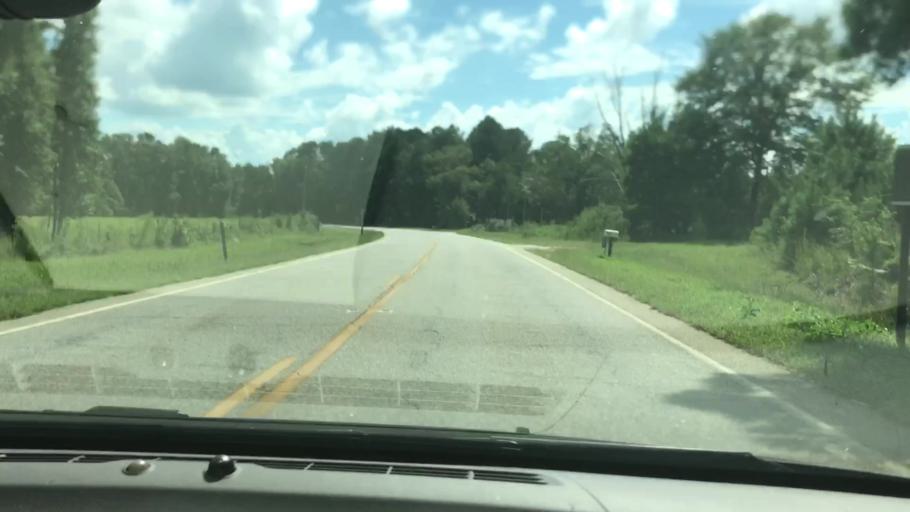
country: US
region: Georgia
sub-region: Clay County
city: Fort Gaines
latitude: 31.6942
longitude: -85.0458
